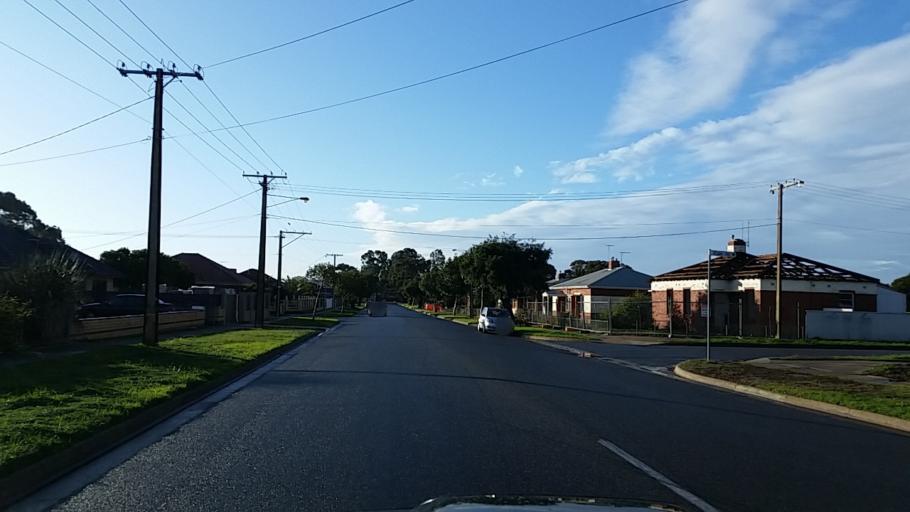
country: AU
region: South Australia
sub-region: Charles Sturt
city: Findon
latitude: -34.9013
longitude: 138.5369
